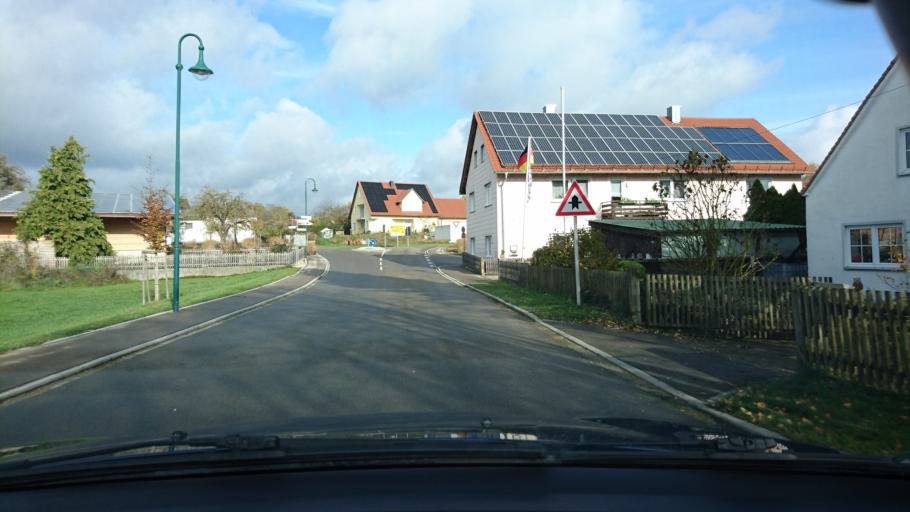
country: DE
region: Bavaria
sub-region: Swabia
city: Amerdingen
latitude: 48.7273
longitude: 10.4857
